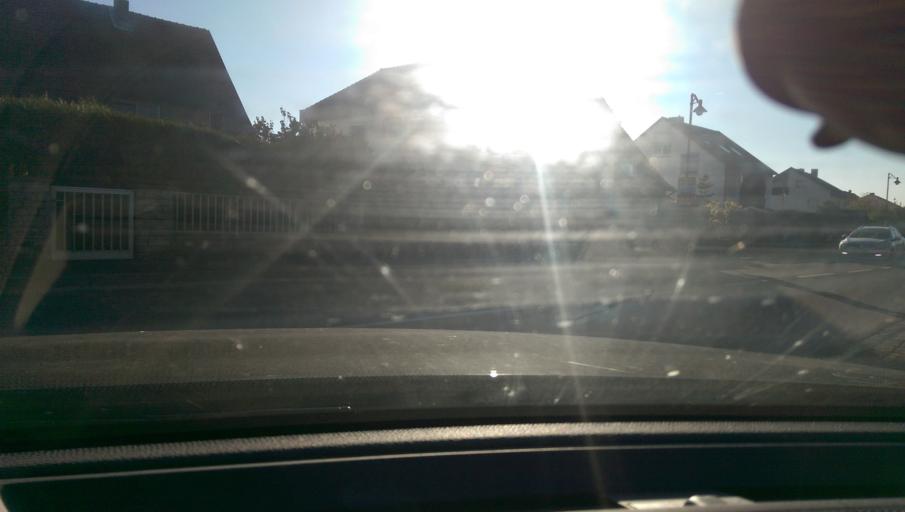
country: DE
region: Bavaria
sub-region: Regierungsbezirk Unterfranken
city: Grafenrheinfeld
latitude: 50.0043
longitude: 10.1926
